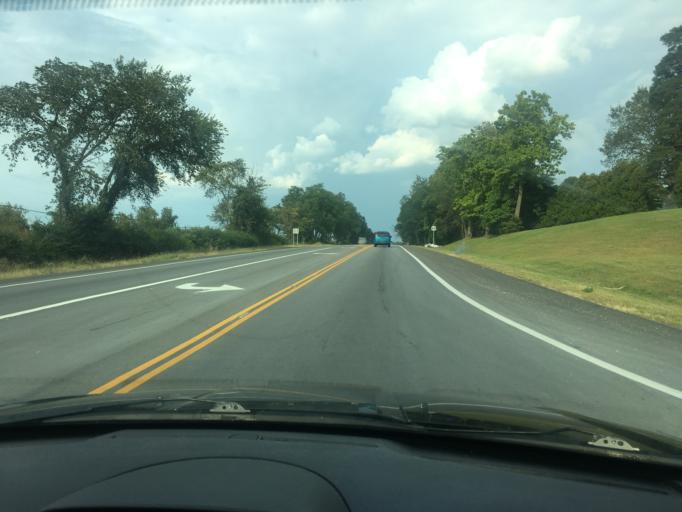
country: US
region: Ohio
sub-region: Champaign County
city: Urbana
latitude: 40.0691
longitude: -83.7724
